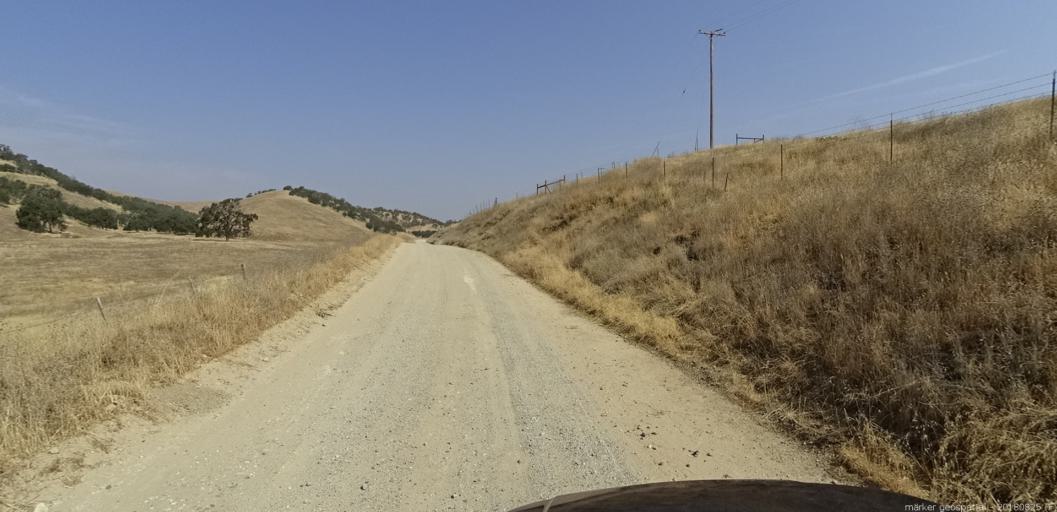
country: US
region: California
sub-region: San Luis Obispo County
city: San Miguel
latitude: 35.8374
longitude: -120.6556
